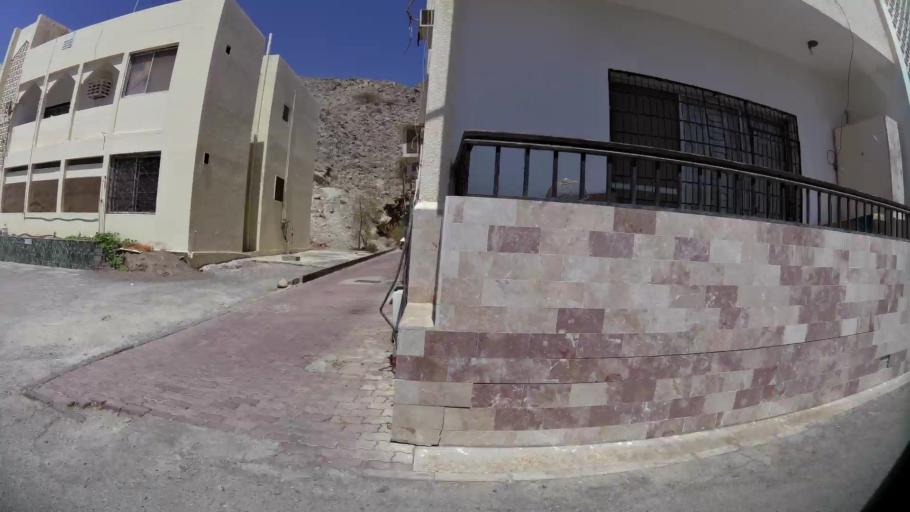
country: OM
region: Muhafazat Masqat
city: Muscat
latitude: 23.5983
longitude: 58.5346
